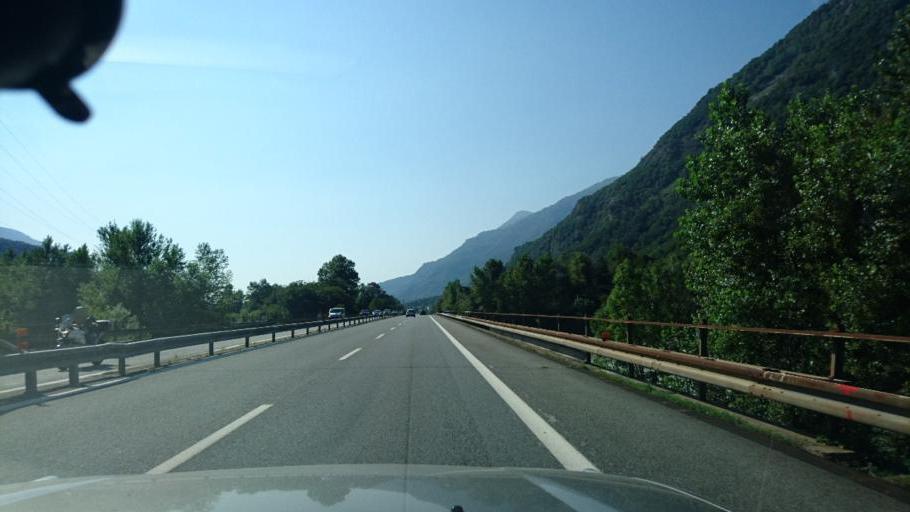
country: IT
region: Piedmont
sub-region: Provincia di Torino
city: Carema
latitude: 45.5817
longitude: 7.7998
